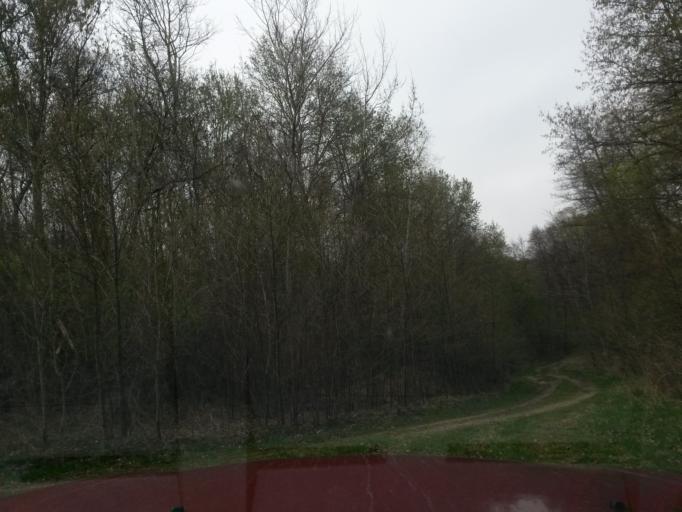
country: SK
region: Kosicky
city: Kosice
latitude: 48.7420
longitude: 21.1184
